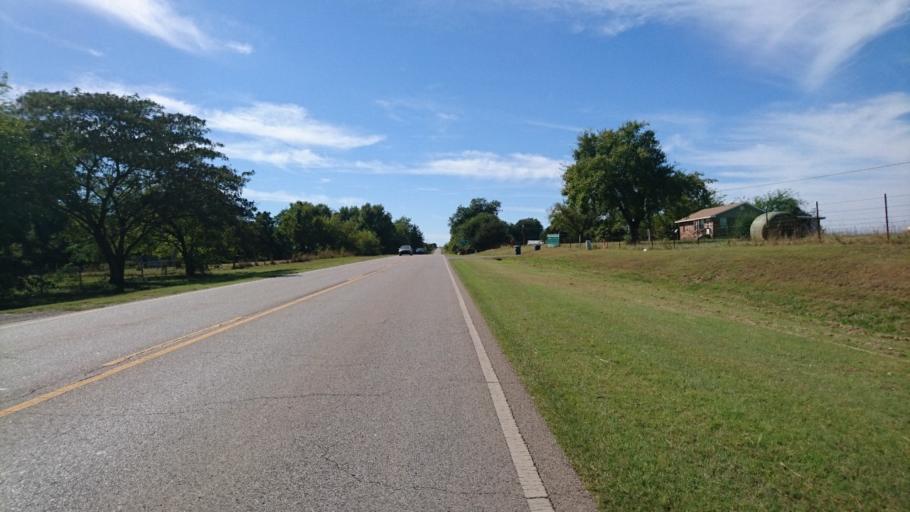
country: US
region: Oklahoma
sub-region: Lincoln County
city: Chandler
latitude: 35.7099
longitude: -96.7731
